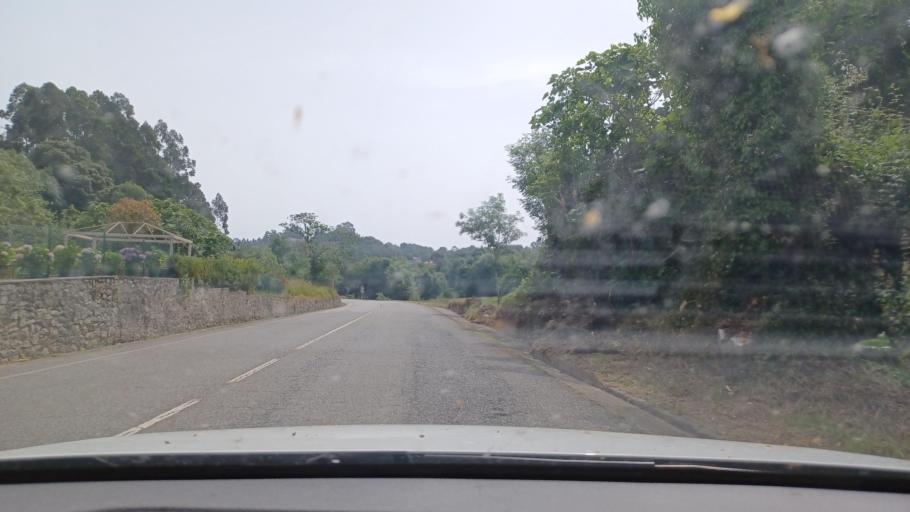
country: ES
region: Asturias
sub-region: Province of Asturias
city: Ribadesella
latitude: 43.4411
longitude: -4.9906
